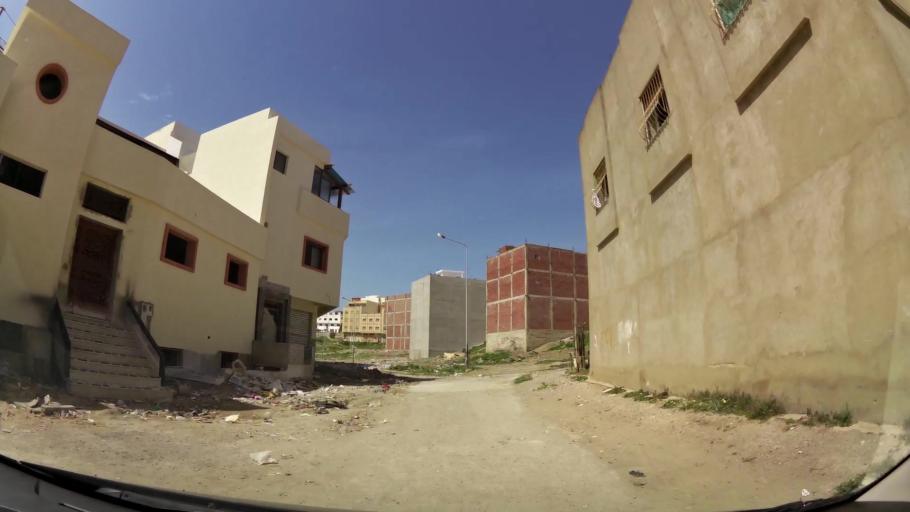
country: MA
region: Tanger-Tetouan
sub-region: Tanger-Assilah
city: Tangier
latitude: 35.7290
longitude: -5.8087
